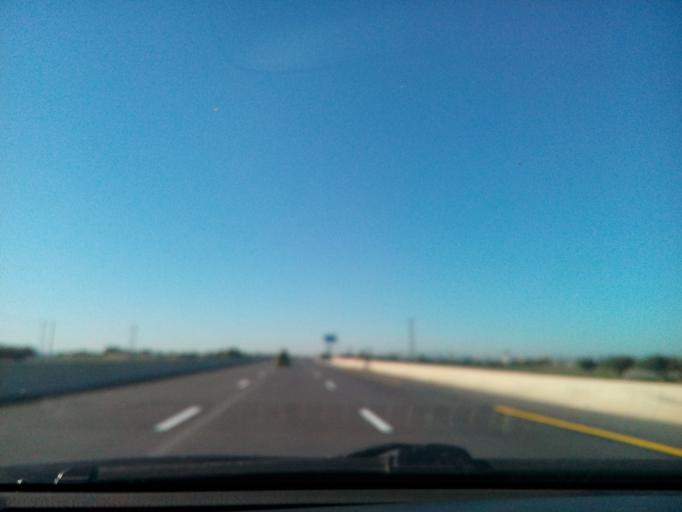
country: DZ
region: Relizane
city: Djidiouia
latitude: 35.9208
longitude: 0.7725
